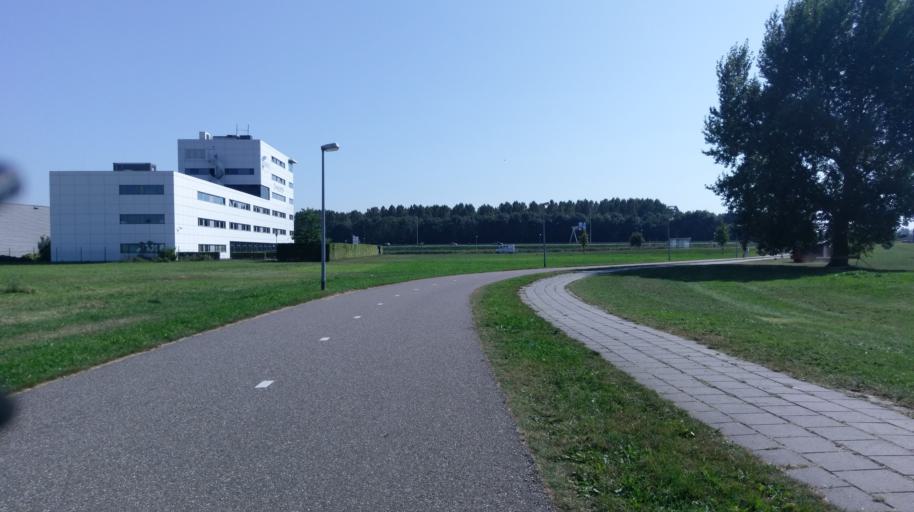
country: NL
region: Flevoland
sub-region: Gemeente Almere
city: Almere Stad
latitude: 52.3554
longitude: 5.2437
